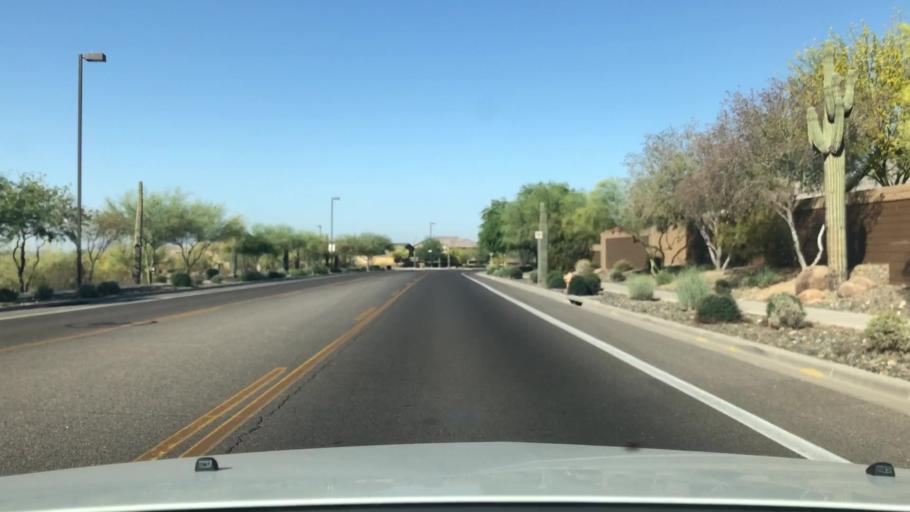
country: US
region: Arizona
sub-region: Maricopa County
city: Anthem
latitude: 33.7311
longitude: -112.0953
